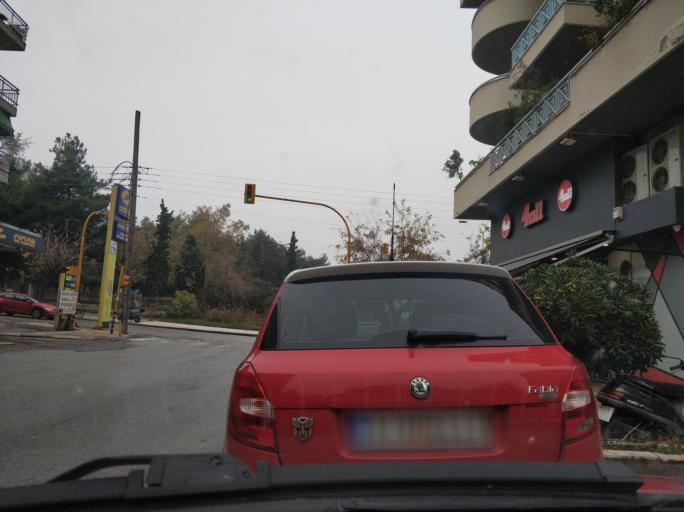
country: GR
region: Central Macedonia
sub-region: Nomos Thessalonikis
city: Pylaia
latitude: 40.5972
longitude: 22.9718
